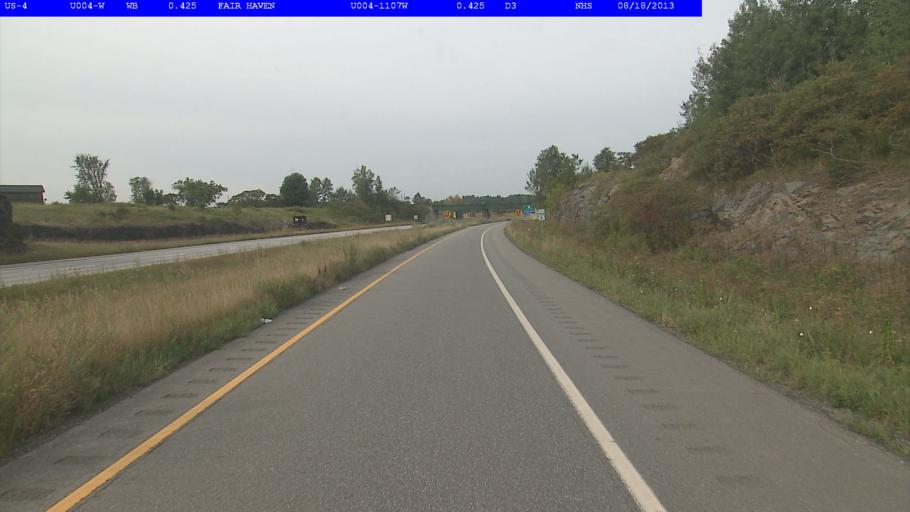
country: US
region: Vermont
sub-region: Rutland County
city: Fair Haven
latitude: 43.5895
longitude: -73.2883
